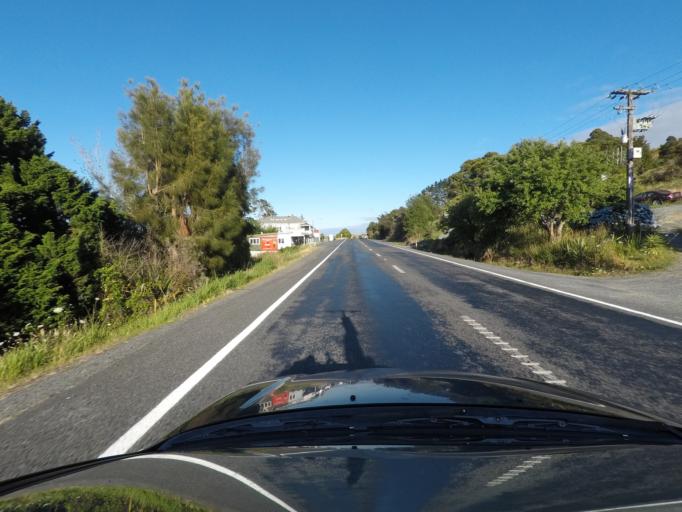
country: NZ
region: Northland
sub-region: Far North District
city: Kawakawa
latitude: -35.4941
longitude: 174.1384
